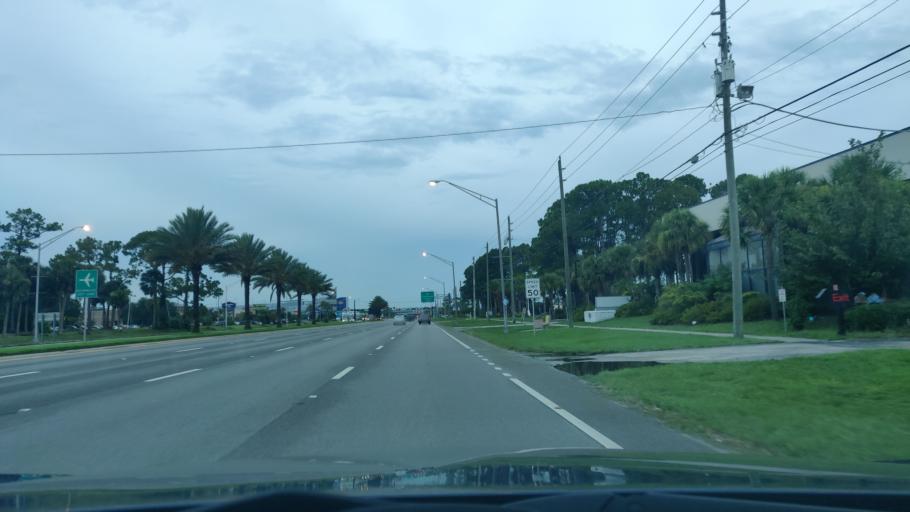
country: US
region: Florida
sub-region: Volusia County
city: Daytona Beach
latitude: 29.1960
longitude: -81.0590
